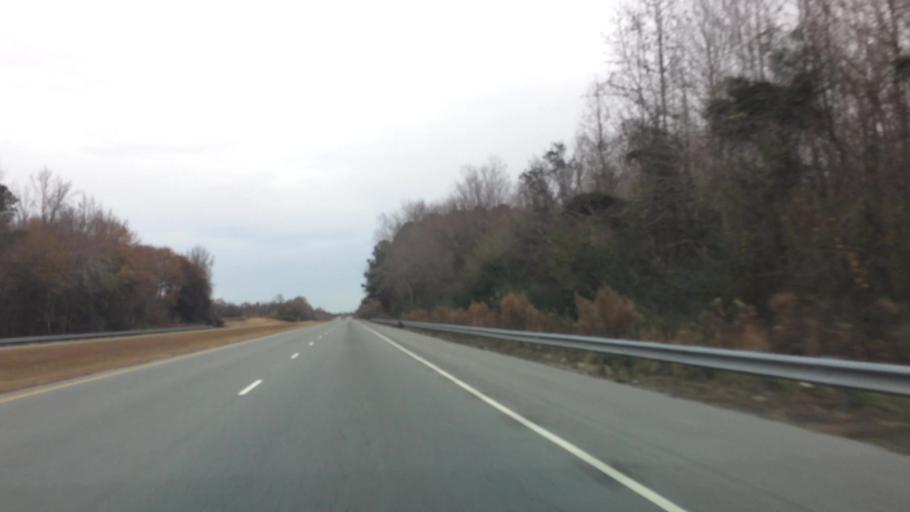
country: US
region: North Carolina
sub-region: Wayne County
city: Mount Olive
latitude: 35.1393
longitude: -78.1345
